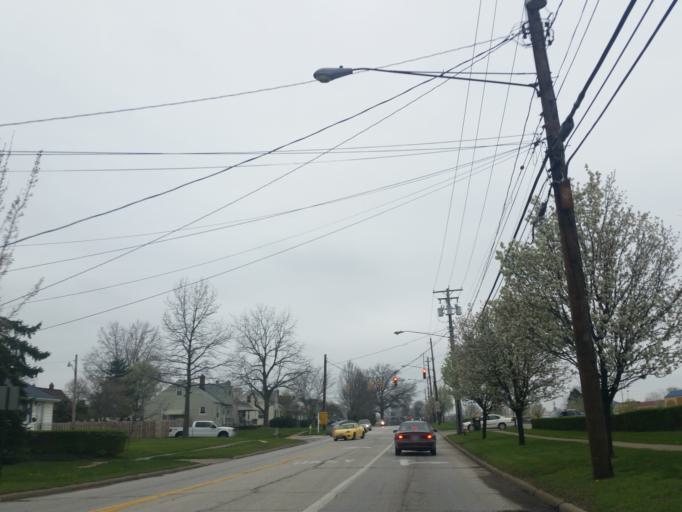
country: US
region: Ohio
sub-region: Cuyahoga County
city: Brooklyn
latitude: 41.4304
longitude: -81.7312
